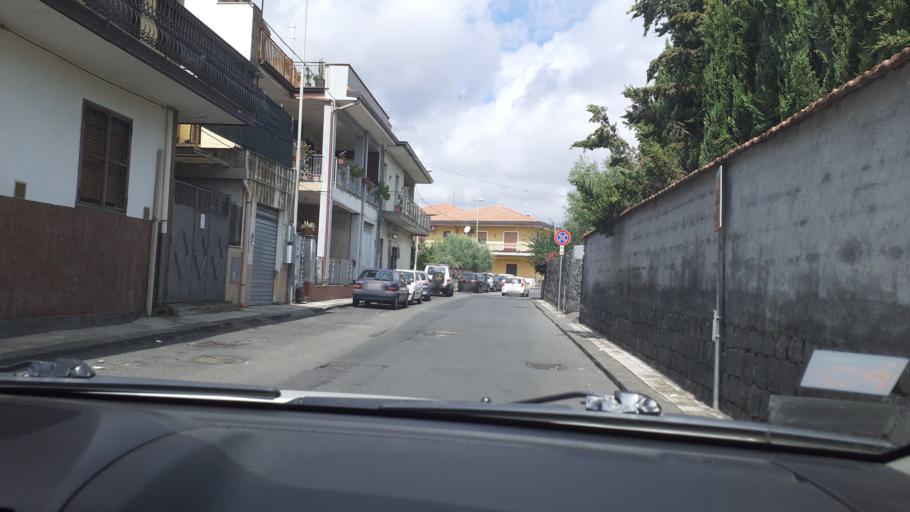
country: IT
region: Sicily
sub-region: Catania
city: San Giovanni la Punta
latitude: 37.5860
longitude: 15.0955
